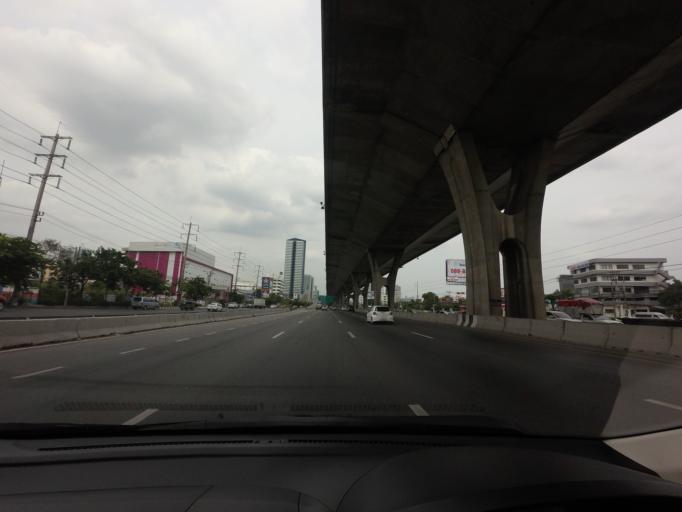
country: TH
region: Bangkok
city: Bang Na
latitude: 13.6693
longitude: 100.6279
